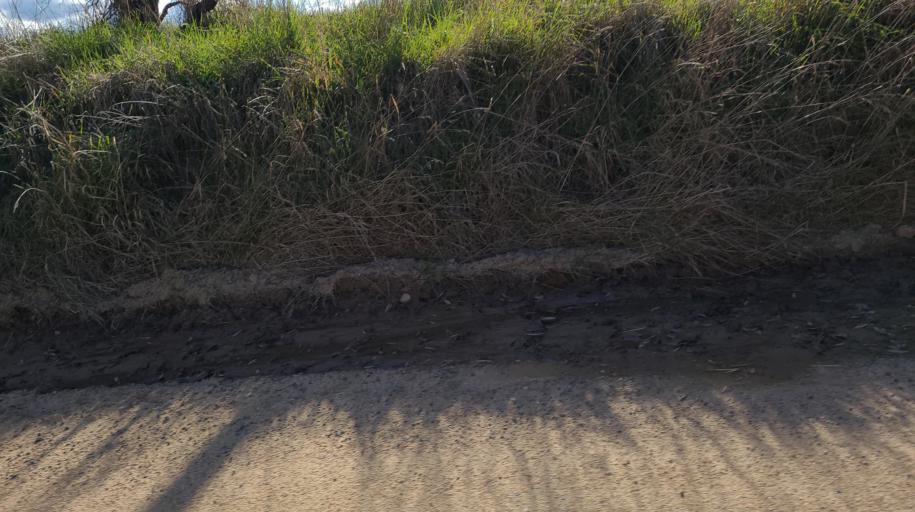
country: AU
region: New South Wales
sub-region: Blayney
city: Millthorpe
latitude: -33.4026
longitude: 149.3081
